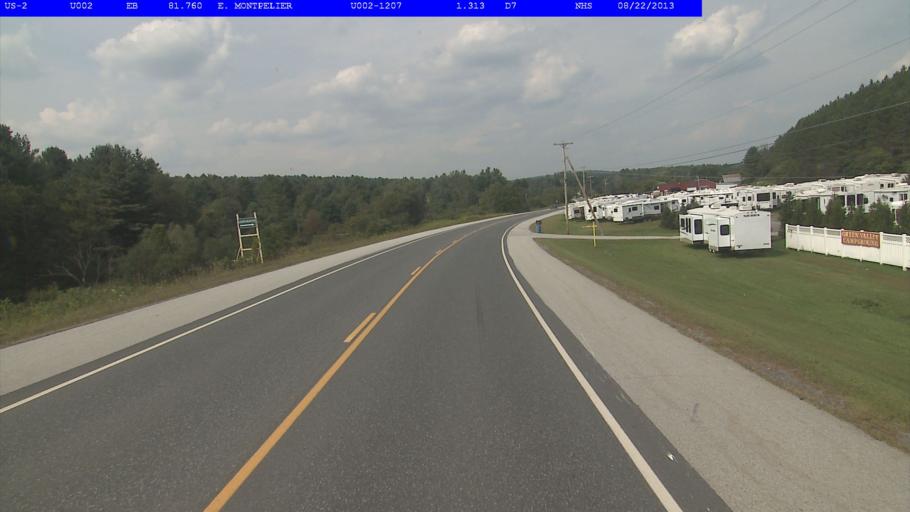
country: US
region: Vermont
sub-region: Washington County
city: Barre
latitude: 44.2520
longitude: -72.5019
